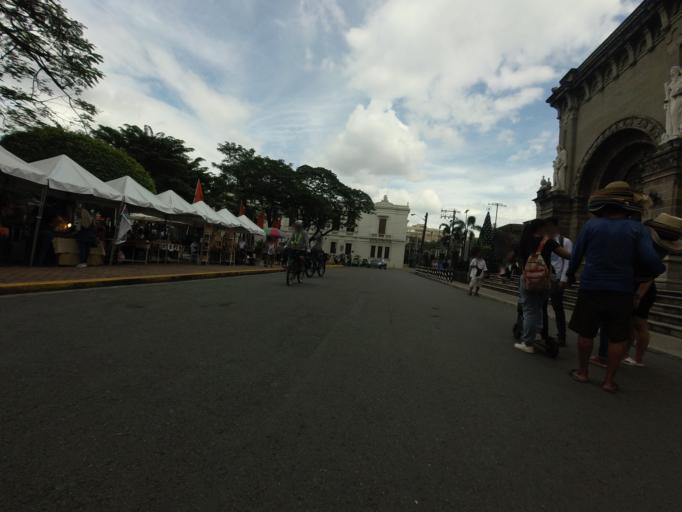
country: PH
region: Metro Manila
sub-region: City of Manila
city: Port Area
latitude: 14.5918
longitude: 120.9732
